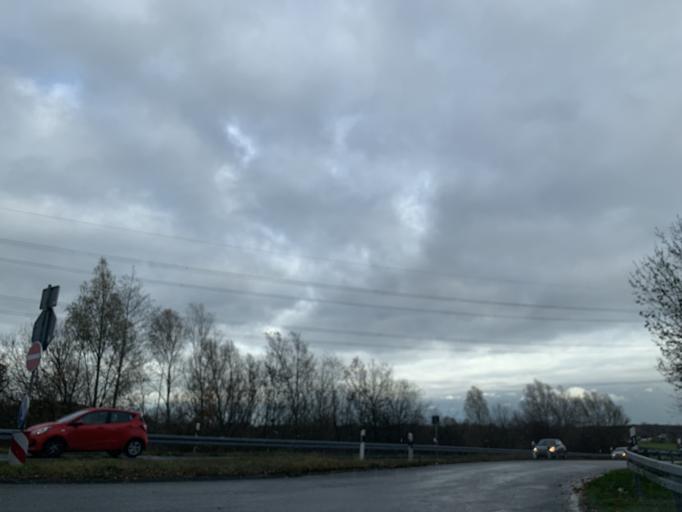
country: DE
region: North Rhine-Westphalia
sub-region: Regierungsbezirk Munster
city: Gronau
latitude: 52.1909
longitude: 6.9754
